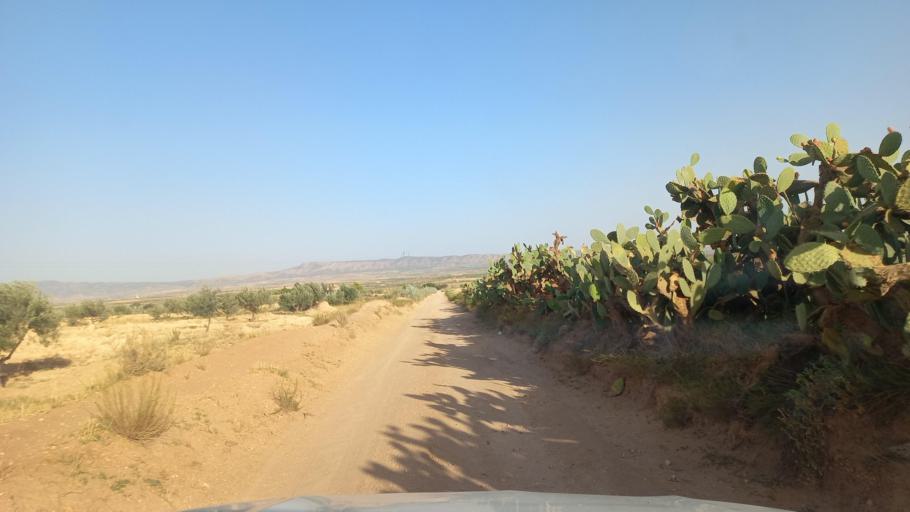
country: TN
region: Al Qasrayn
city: Sbiba
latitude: 35.3664
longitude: 9.0136
